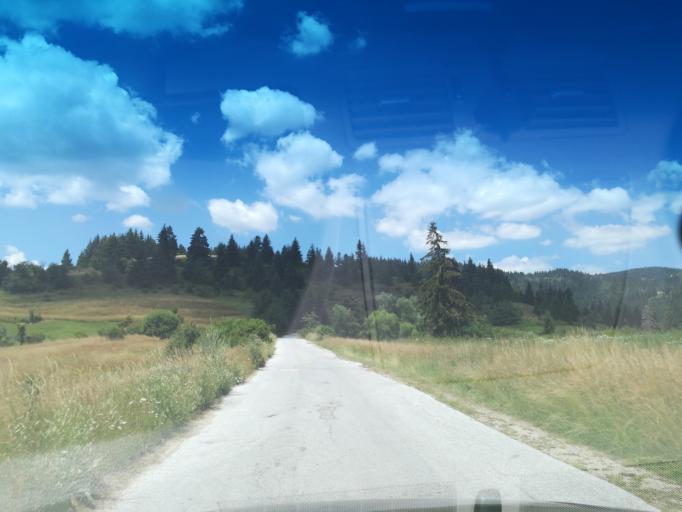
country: BG
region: Smolyan
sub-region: Obshtina Chepelare
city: Chepelare
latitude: 41.6743
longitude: 24.7761
